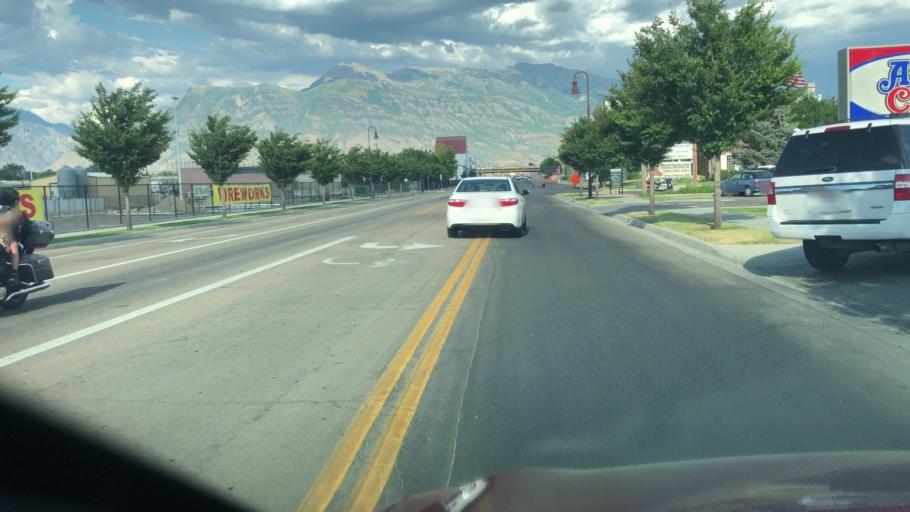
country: US
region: Utah
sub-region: Utah County
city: Lehi
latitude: 40.3881
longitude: -111.8408
